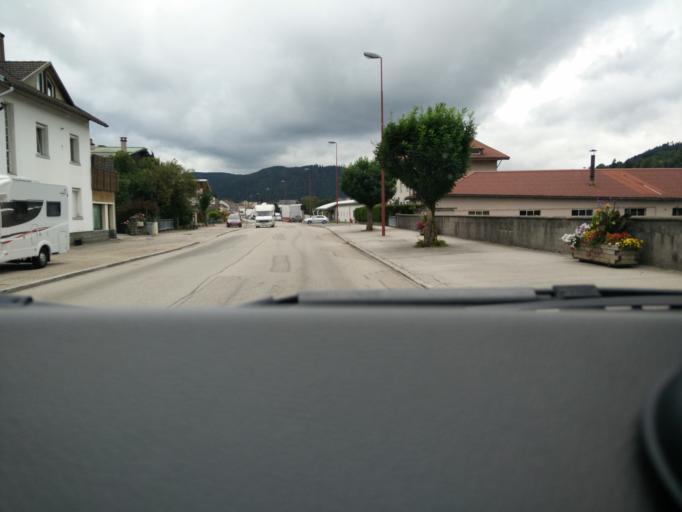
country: FR
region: Lorraine
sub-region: Departement des Vosges
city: Gerardmer
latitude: 48.0745
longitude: 6.8788
